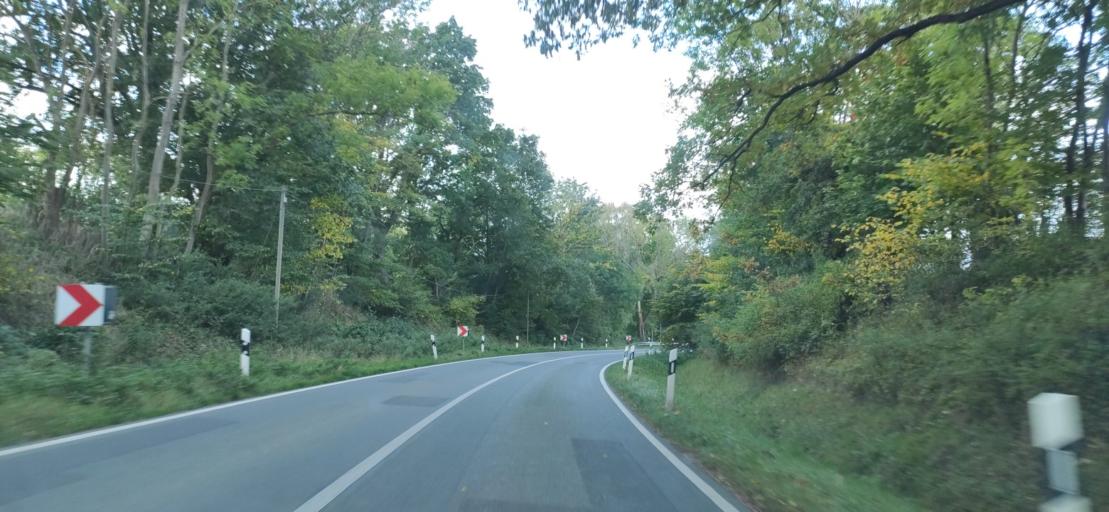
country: DE
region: Mecklenburg-Vorpommern
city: Grabowhofe
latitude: 53.6476
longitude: 12.5383
